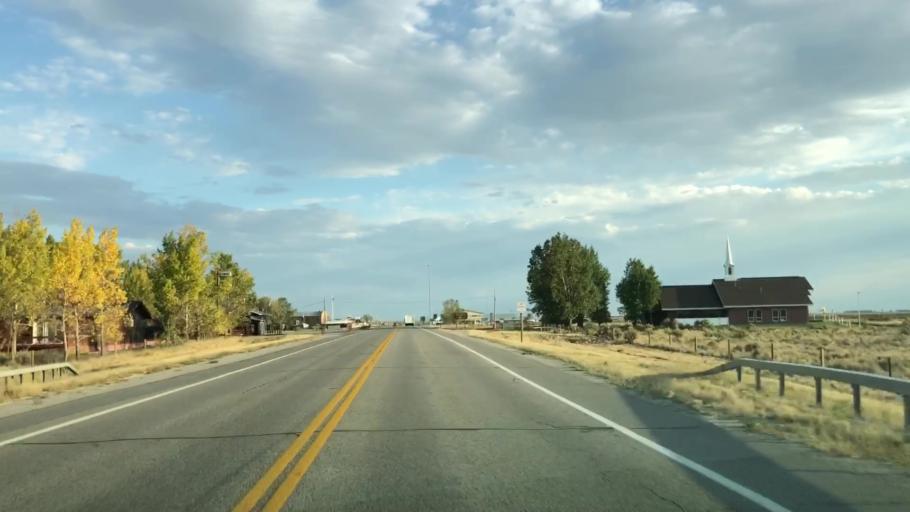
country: US
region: Wyoming
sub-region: Sweetwater County
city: North Rock Springs
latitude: 42.1130
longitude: -109.4504
